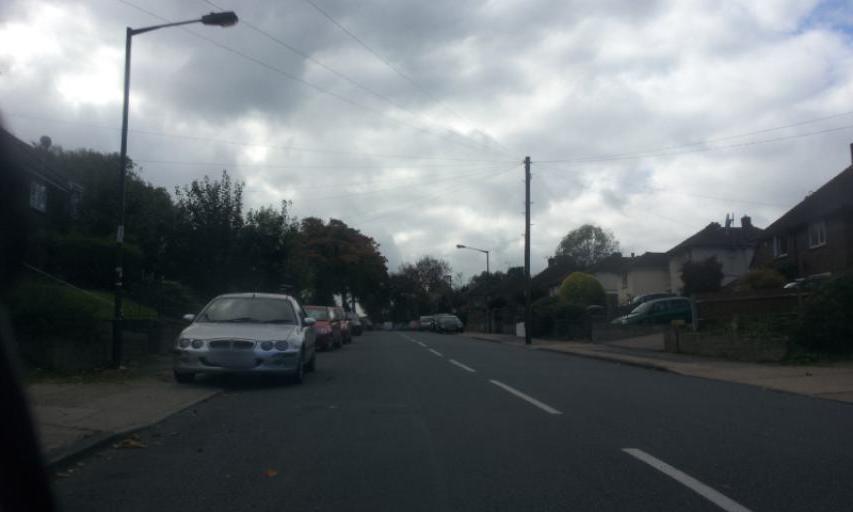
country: GB
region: England
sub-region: Kent
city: Chatham
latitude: 51.3555
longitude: 0.5264
